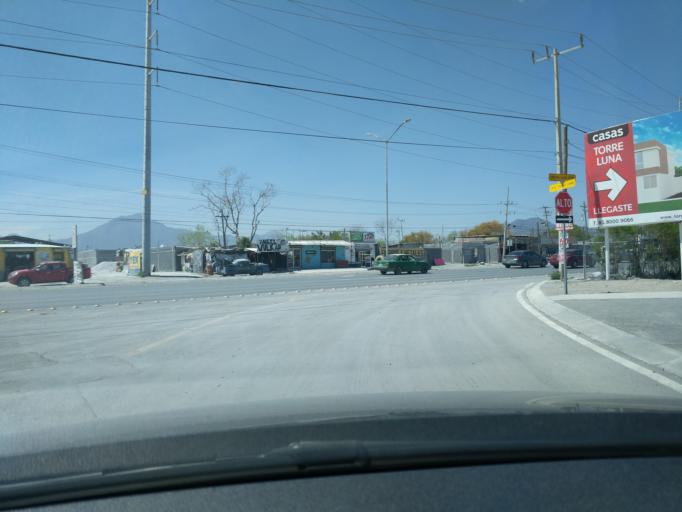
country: MX
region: Nuevo Leon
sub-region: Salinas Victoria
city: Emiliano Zapata
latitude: 25.9099
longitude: -100.2663
